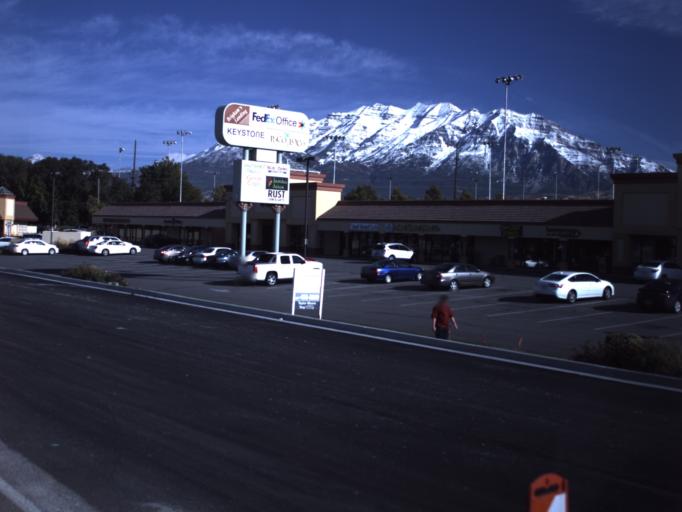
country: US
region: Utah
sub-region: Utah County
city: Provo
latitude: 40.2571
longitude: -111.6610
